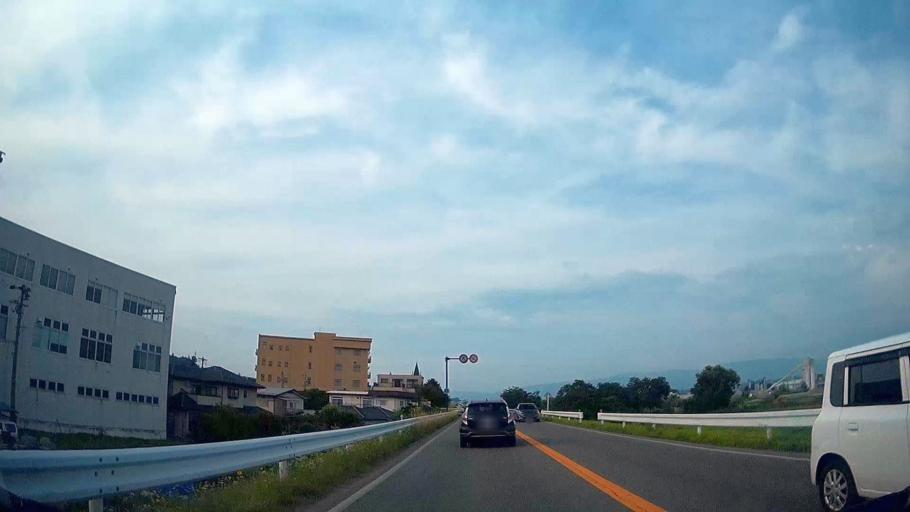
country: JP
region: Nagano
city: Ina
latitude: 35.8226
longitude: 137.9479
